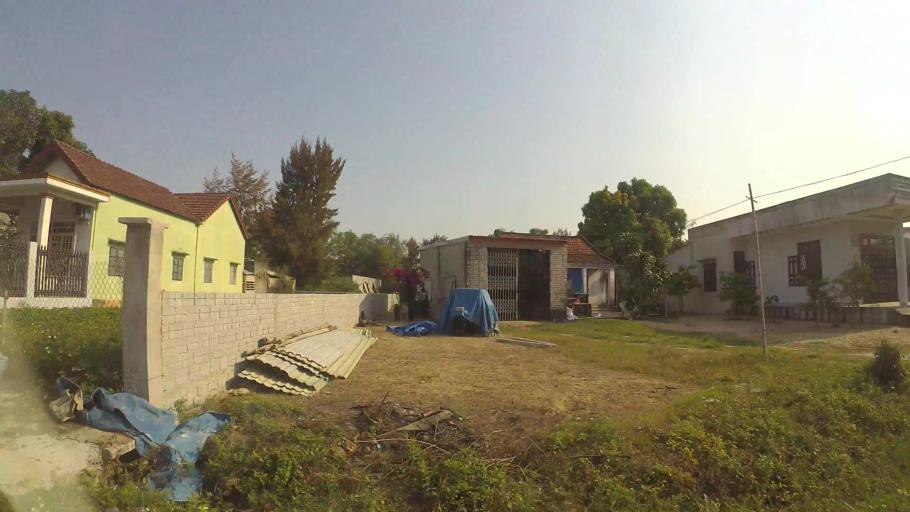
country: VN
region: Quang Nam
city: Quang Nam
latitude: 15.9484
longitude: 108.2556
